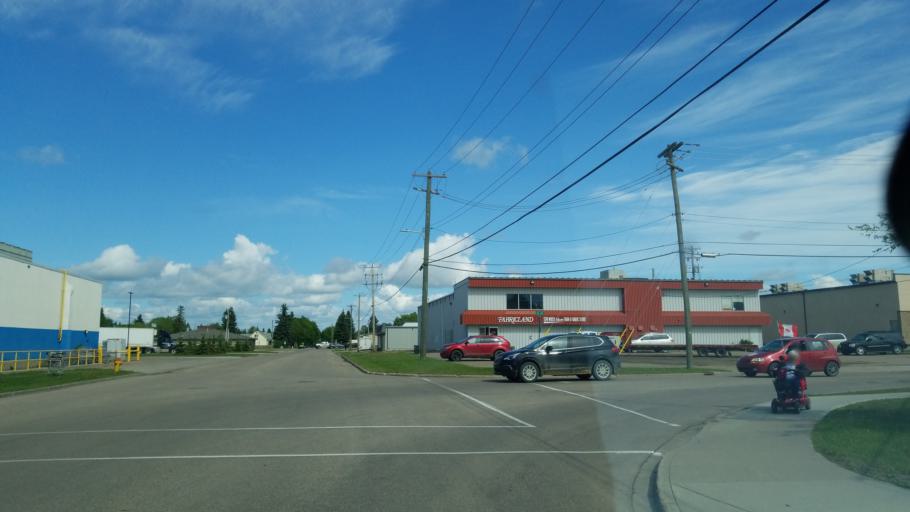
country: CA
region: Saskatchewan
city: Lloydminster
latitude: 53.2752
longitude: -110.0089
